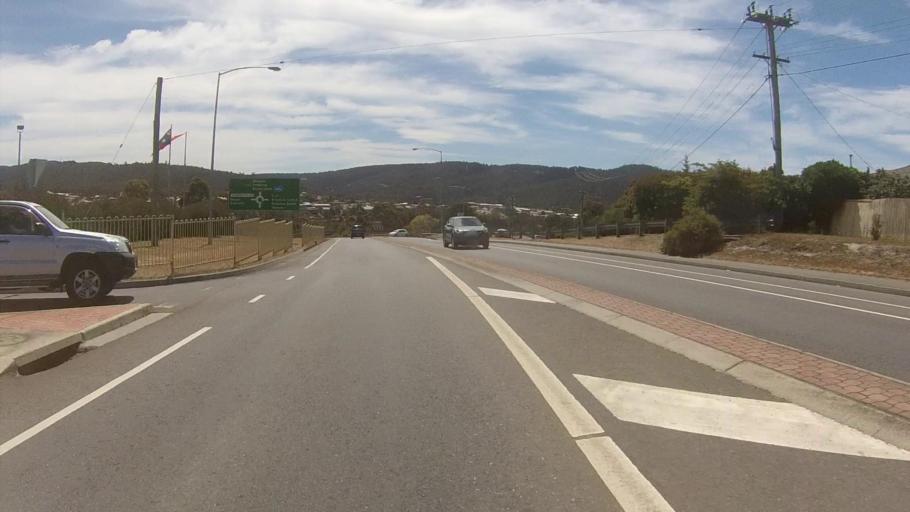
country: AU
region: Tasmania
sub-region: Kingborough
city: Kingston
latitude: -42.9768
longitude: 147.3035
